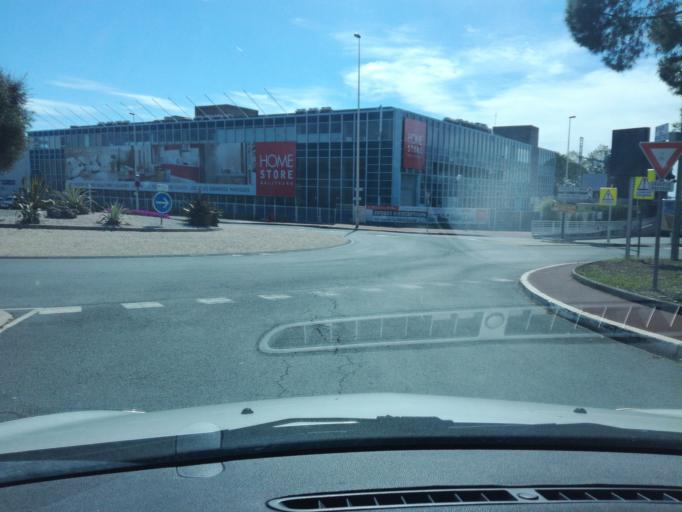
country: FR
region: Provence-Alpes-Cote d'Azur
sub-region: Departement des Alpes-Maritimes
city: Mandelieu-la-Napoule
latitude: 43.5432
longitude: 6.9596
